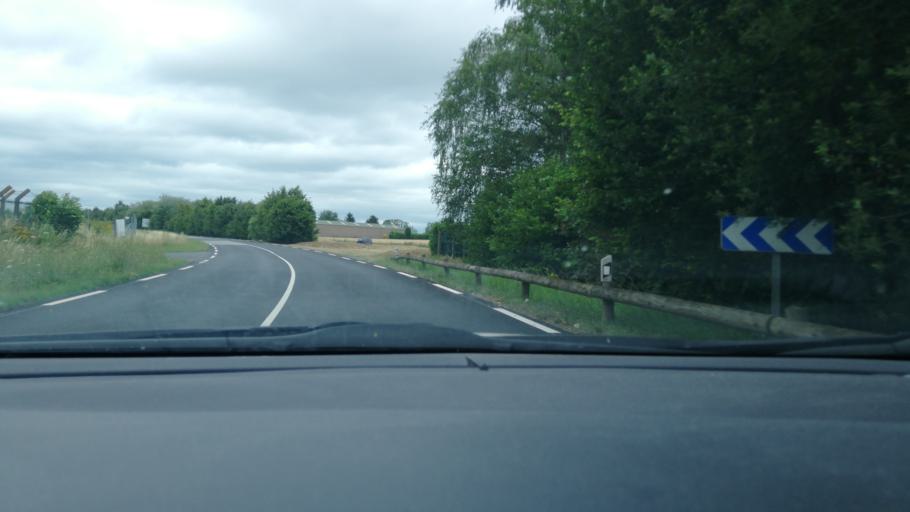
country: FR
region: Ile-de-France
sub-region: Departement du Val-d'Oise
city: Ennery
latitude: 49.1023
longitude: 2.1258
